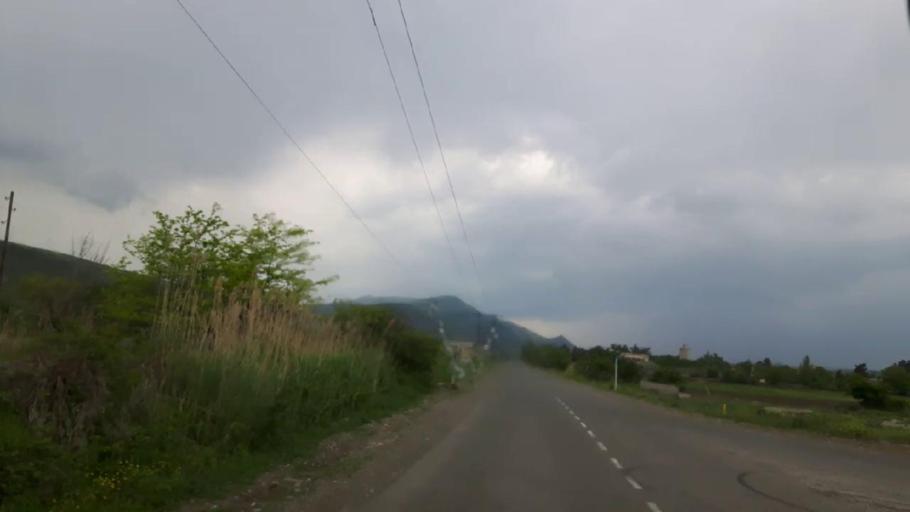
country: GE
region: Shida Kartli
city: Gori
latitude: 41.9642
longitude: 44.1690
